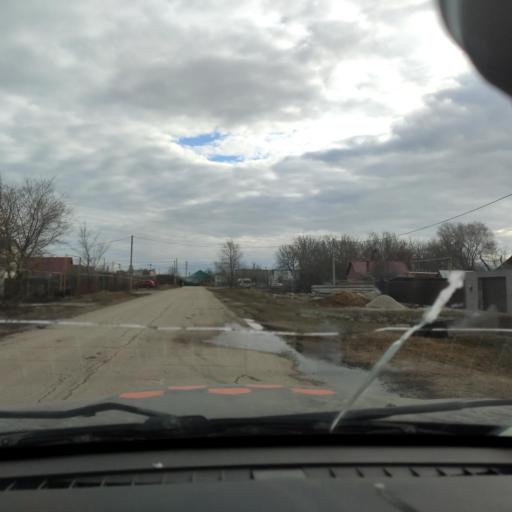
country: RU
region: Samara
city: Tol'yatti
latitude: 53.5716
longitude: 49.3140
